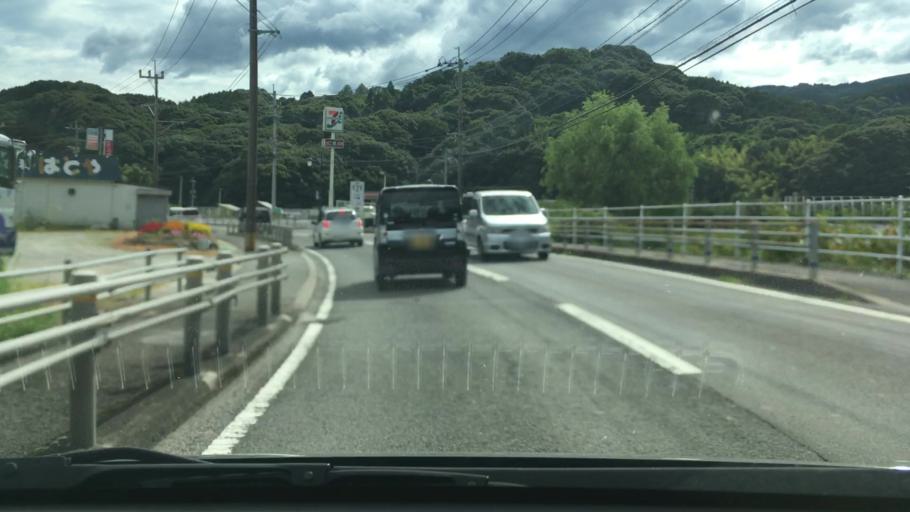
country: JP
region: Nagasaki
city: Togitsu
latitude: 32.9147
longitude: 129.7852
